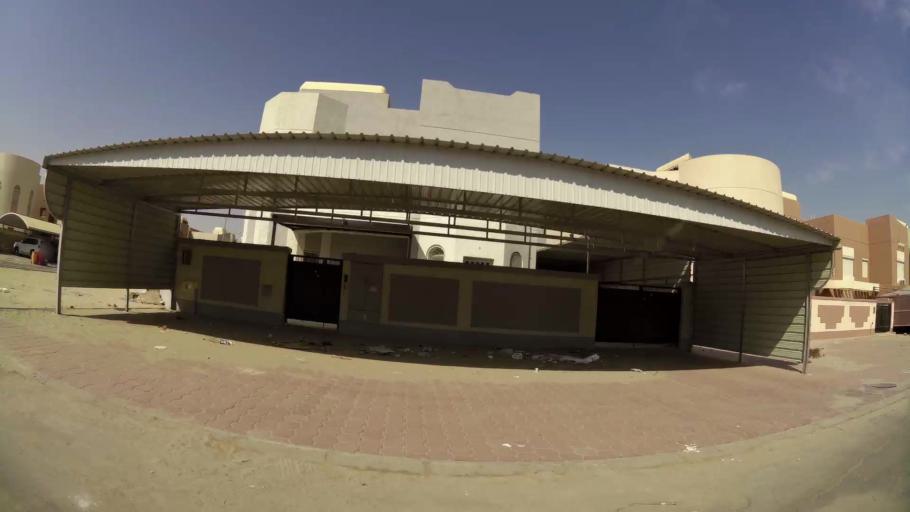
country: KW
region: Al Ahmadi
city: Al Wafrah
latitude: 28.8035
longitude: 48.0648
